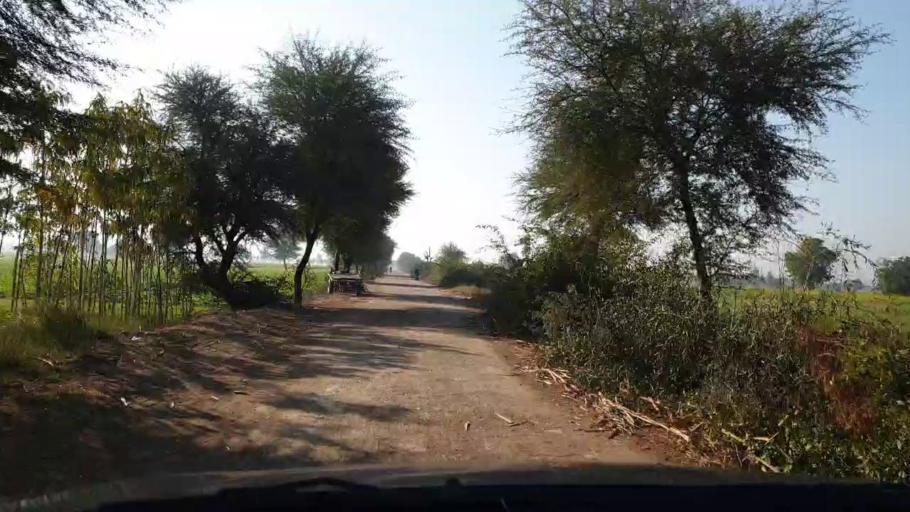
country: PK
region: Sindh
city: Jhol
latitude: 25.9373
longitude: 68.8655
